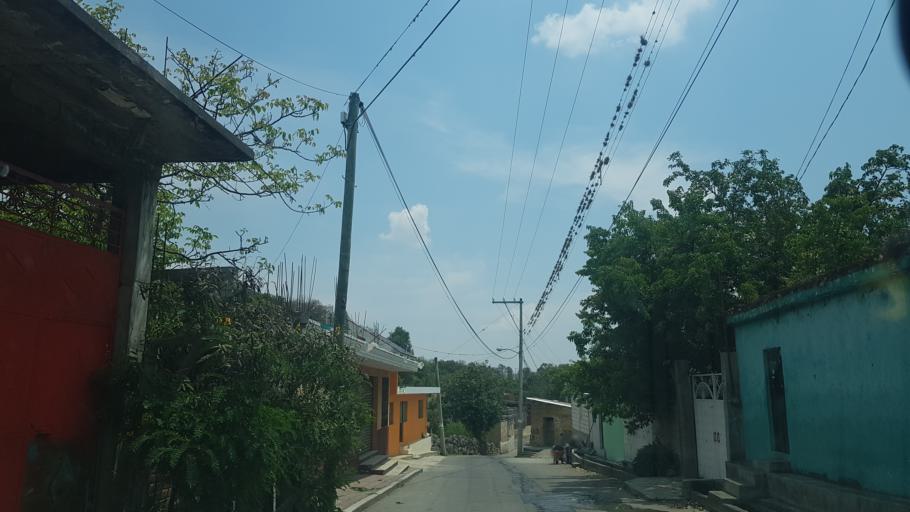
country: MX
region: Puebla
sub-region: Tochimilco
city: La Magdalena Yancuitlalpan
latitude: 18.8876
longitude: -98.6086
